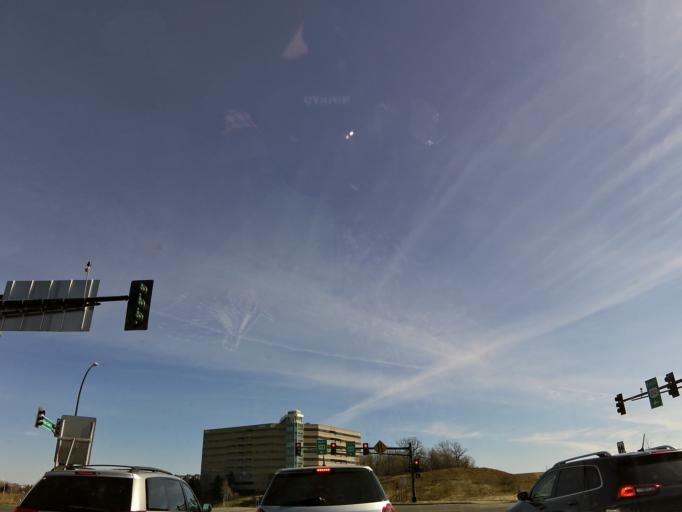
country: US
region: Minnesota
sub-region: Hennepin County
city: Eden Prairie
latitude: 44.8657
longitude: -93.4193
